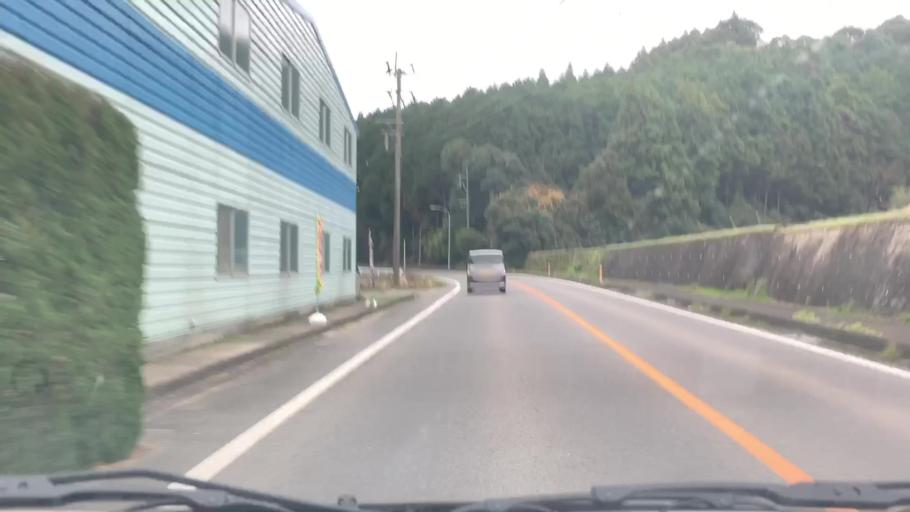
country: JP
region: Saga Prefecture
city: Ureshinomachi-shimojuku
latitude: 33.0910
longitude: 130.0077
